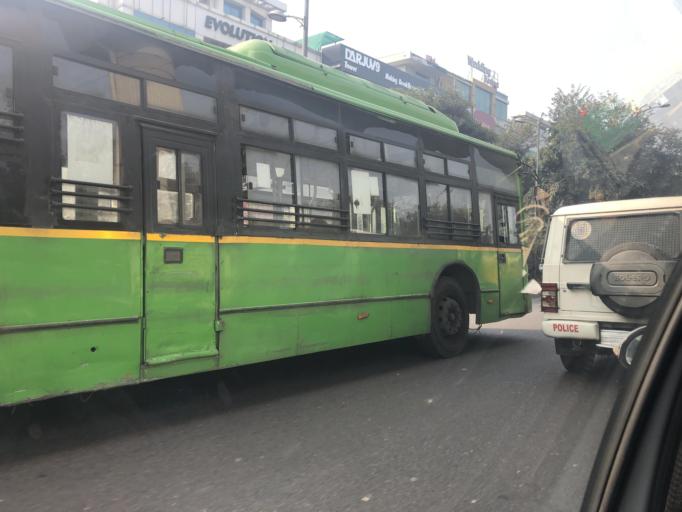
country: IN
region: NCT
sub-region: North West Delhi
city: Pitampura
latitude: 28.6752
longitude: 77.1281
